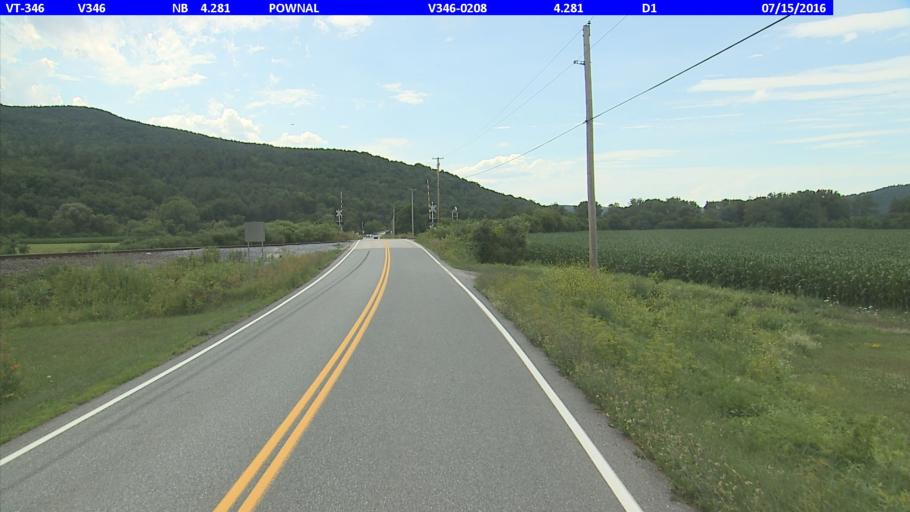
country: US
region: Vermont
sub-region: Bennington County
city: Bennington
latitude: 42.8089
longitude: -73.2797
